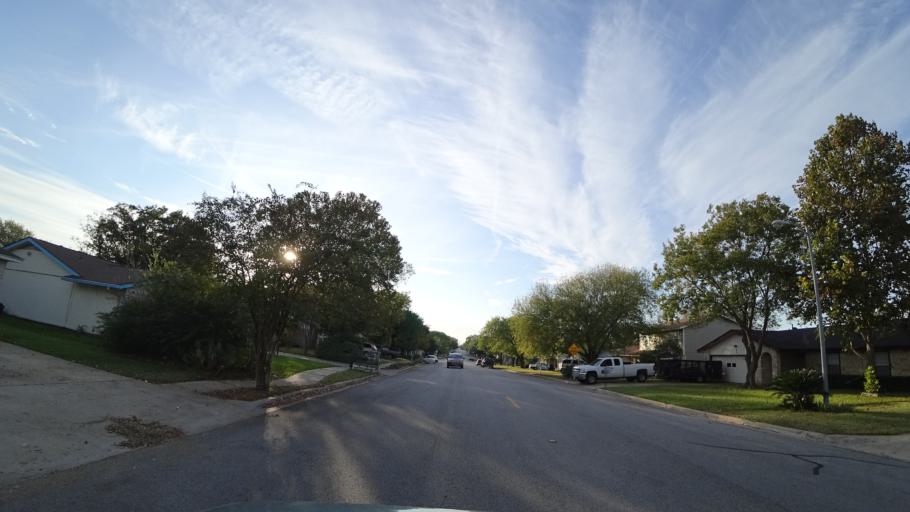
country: US
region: Texas
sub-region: Williamson County
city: Round Rock
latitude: 30.5024
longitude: -97.6681
